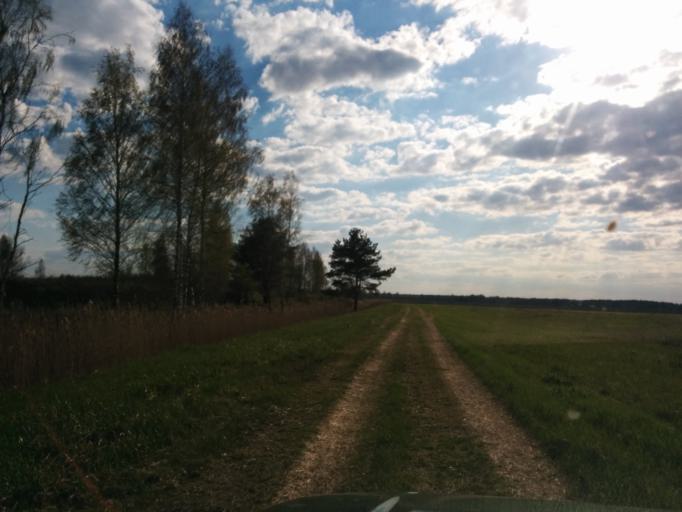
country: LV
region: Jelgava
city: Jelgava
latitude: 56.6818
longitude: 23.6980
